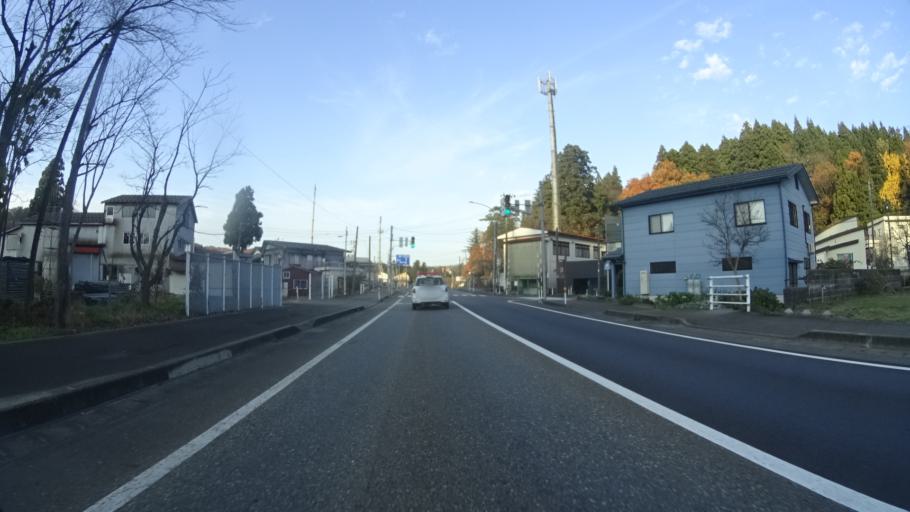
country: JP
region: Niigata
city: Nagaoka
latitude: 37.4323
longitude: 138.7280
